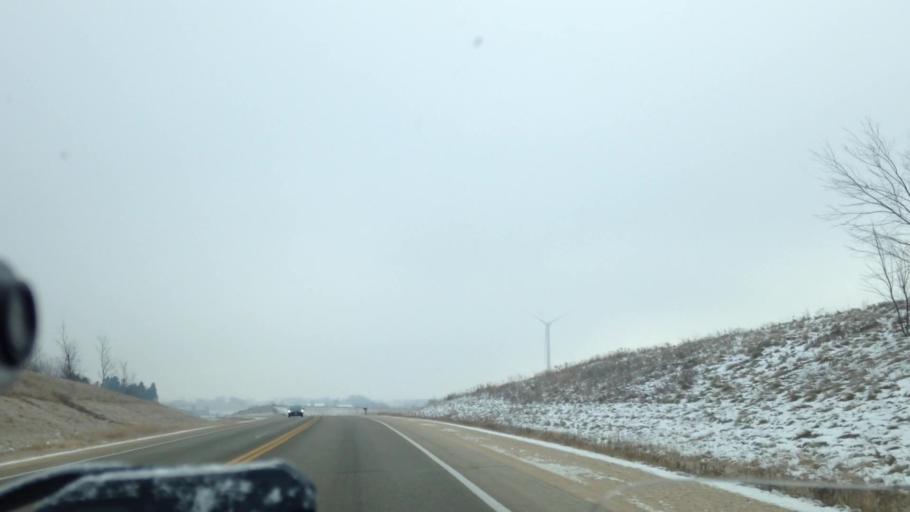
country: US
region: Wisconsin
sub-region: Dodge County
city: Theresa
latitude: 43.4376
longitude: -88.4755
